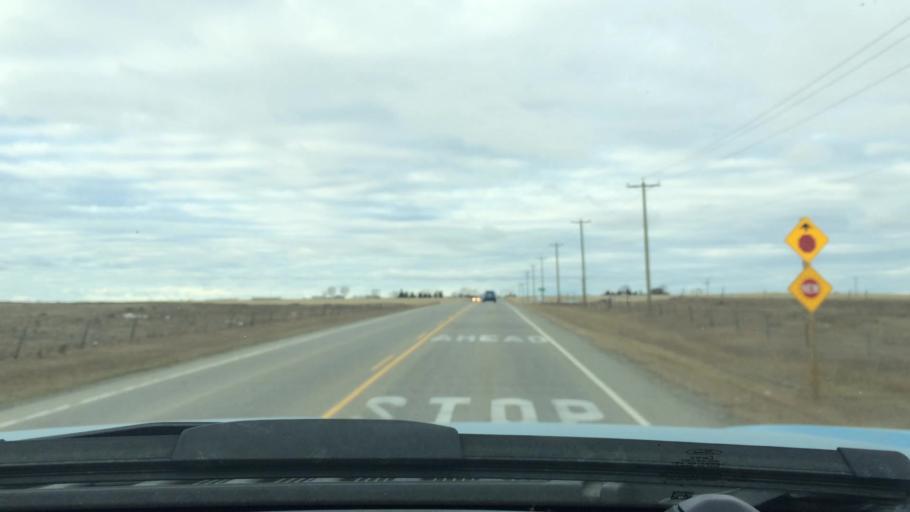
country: CA
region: Alberta
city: Airdrie
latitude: 51.2126
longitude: -114.0207
